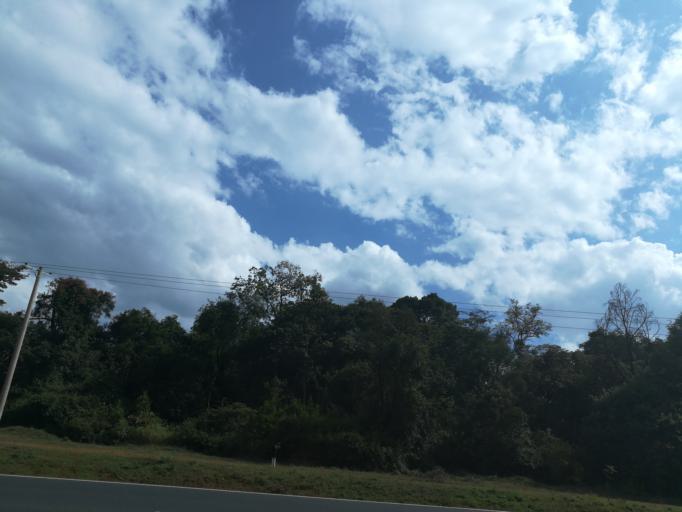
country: KE
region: Nairobi Area
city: Nairobi
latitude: -1.3226
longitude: 36.7374
